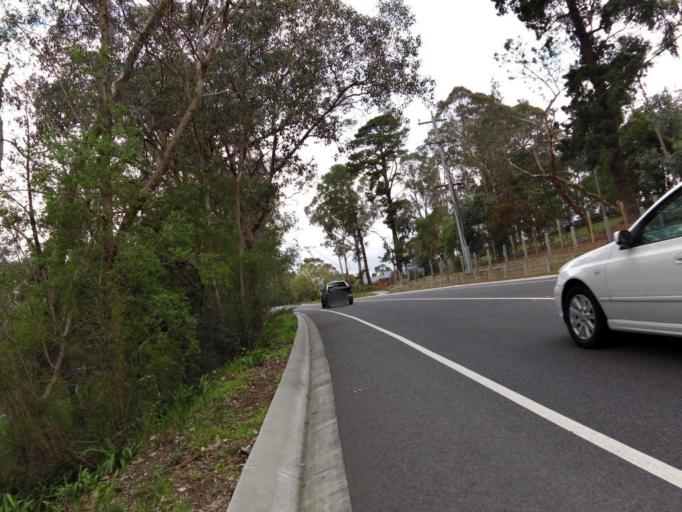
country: AU
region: Victoria
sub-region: Manningham
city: Park Orchards
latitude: -37.7906
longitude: 145.1982
